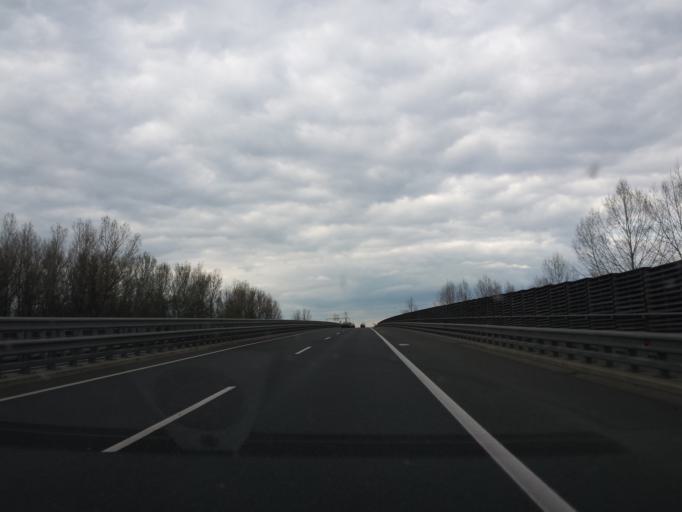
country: AT
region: Lower Austria
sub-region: Politischer Bezirk Sankt Polten
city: Traismauer
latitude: 48.3813
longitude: 15.7172
